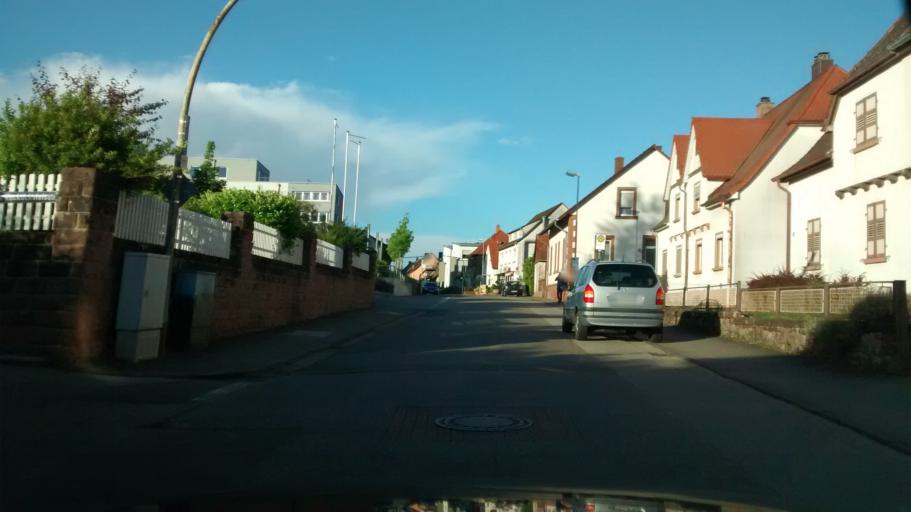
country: DE
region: Rheinland-Pfalz
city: Dahn
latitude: 49.1530
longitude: 7.7846
